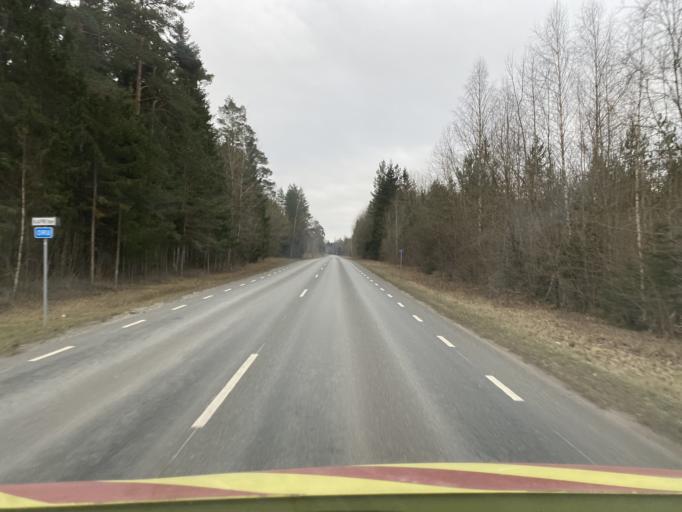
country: EE
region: Laeaene
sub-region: Ridala Parish
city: Uuemoisa
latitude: 59.0086
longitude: 23.6920
